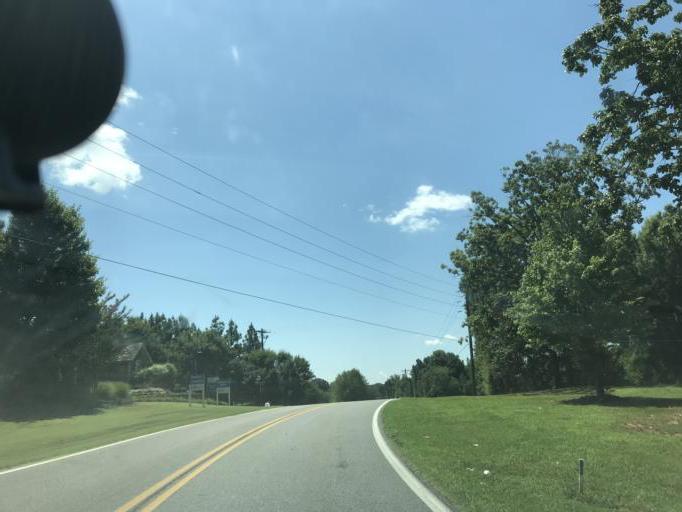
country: US
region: Georgia
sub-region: Forsyth County
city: Cumming
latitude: 34.2947
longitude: -84.0250
